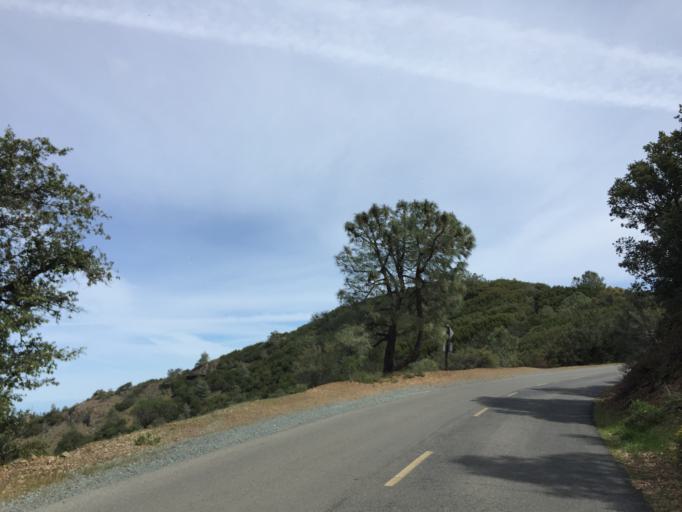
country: US
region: California
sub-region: Contra Costa County
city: Diablo
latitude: 37.8813
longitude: -121.9186
